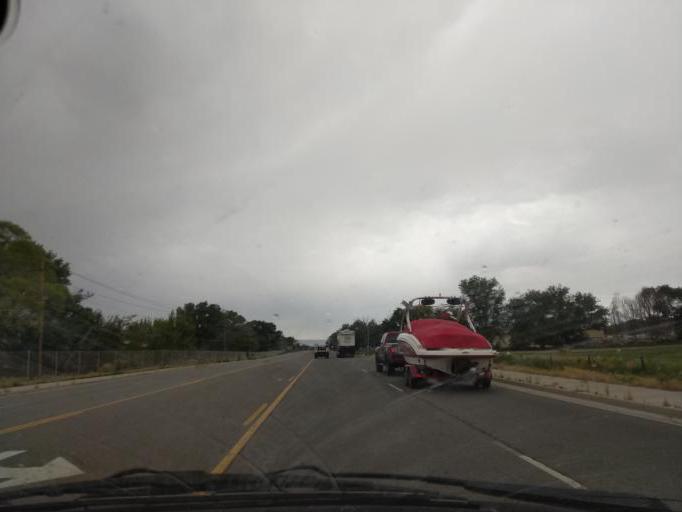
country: US
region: Colorado
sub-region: Delta County
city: Delta
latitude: 38.7632
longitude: -108.0800
